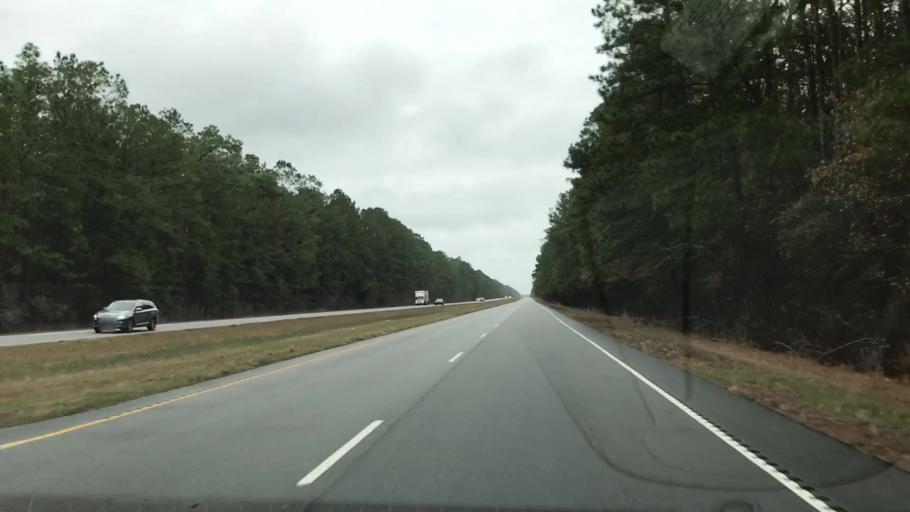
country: US
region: South Carolina
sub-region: Charleston County
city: Awendaw
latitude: 33.1451
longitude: -79.4366
